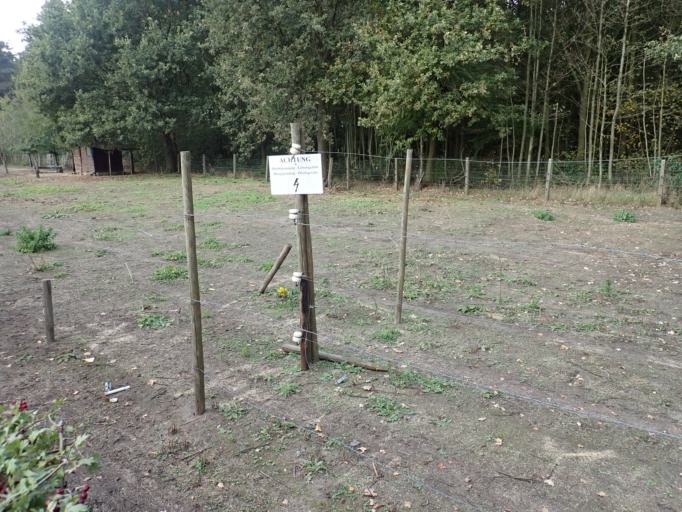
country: BE
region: Flanders
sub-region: Provincie Oost-Vlaanderen
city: Stekene
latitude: 51.2415
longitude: 4.0433
